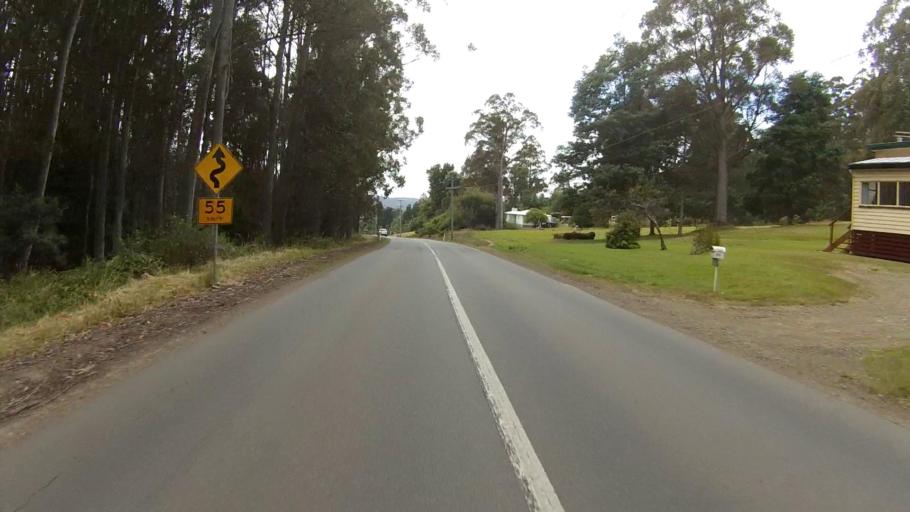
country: AU
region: Tasmania
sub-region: Kingborough
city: Kettering
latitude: -43.1165
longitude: 147.1894
